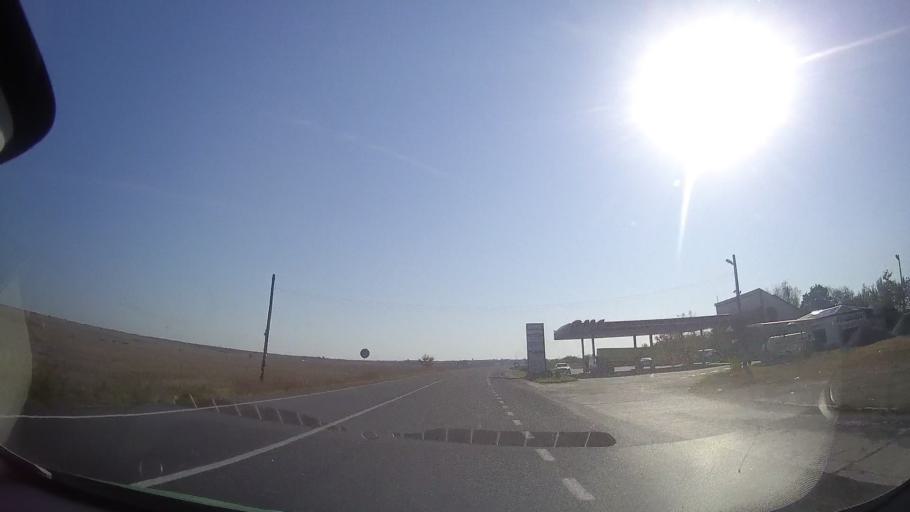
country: RO
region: Timis
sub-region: Comuna Topolovatu Mare
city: Topolovatu Mare
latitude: 45.7836
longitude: 21.5993
